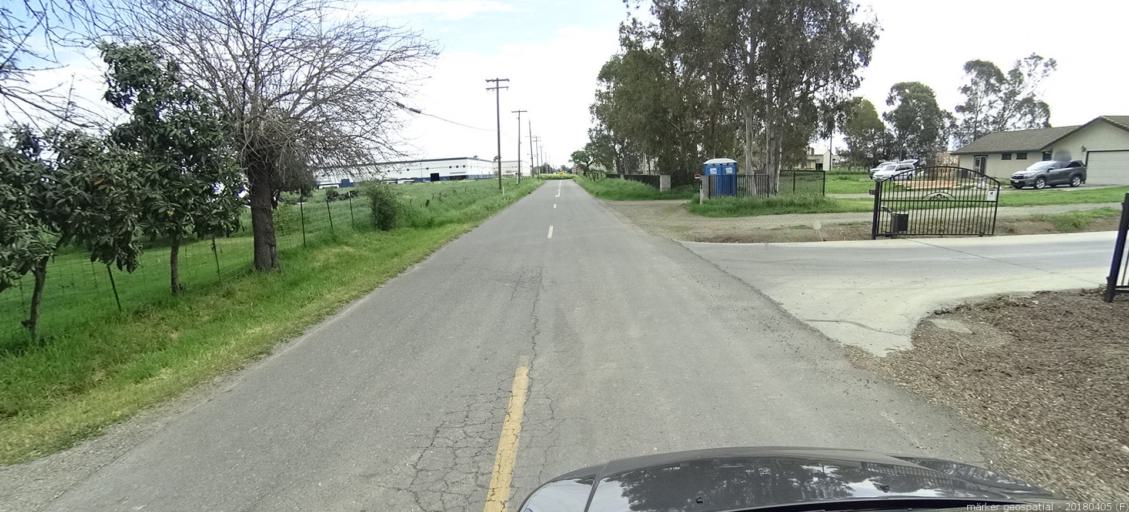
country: US
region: California
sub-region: Sacramento County
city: Galt
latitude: 38.2681
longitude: -121.3143
